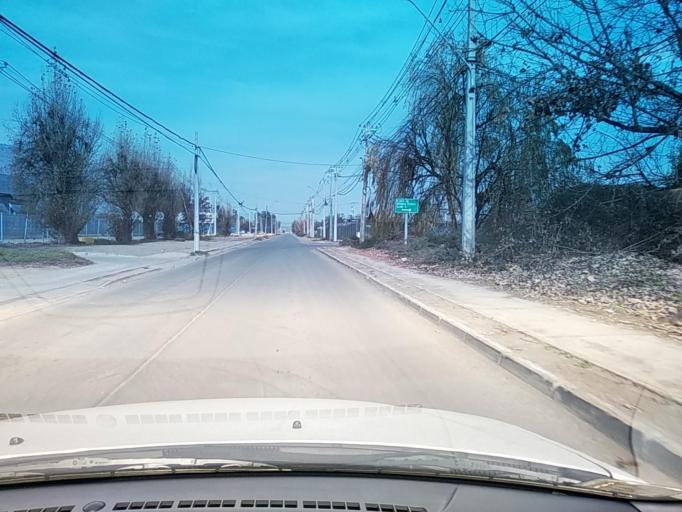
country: CL
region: Santiago Metropolitan
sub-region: Provincia de Chacabuco
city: Chicureo Abajo
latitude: -33.3070
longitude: -70.7170
